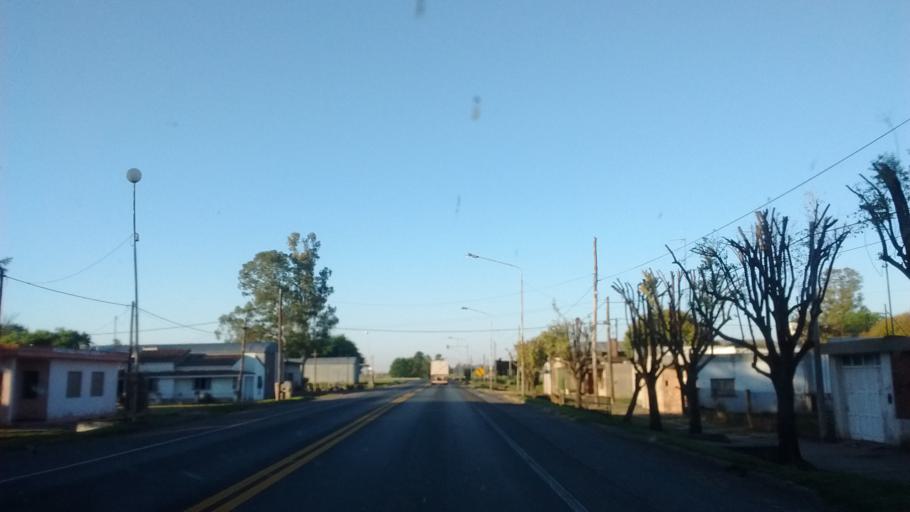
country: AR
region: Santa Fe
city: Firmat
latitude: -33.3518
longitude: -61.4468
